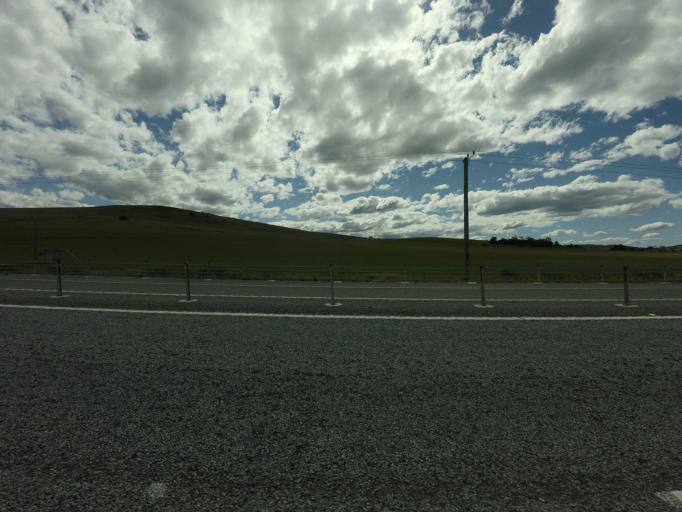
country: AU
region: Tasmania
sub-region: Northern Midlands
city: Evandale
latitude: -42.1047
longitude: 147.4487
